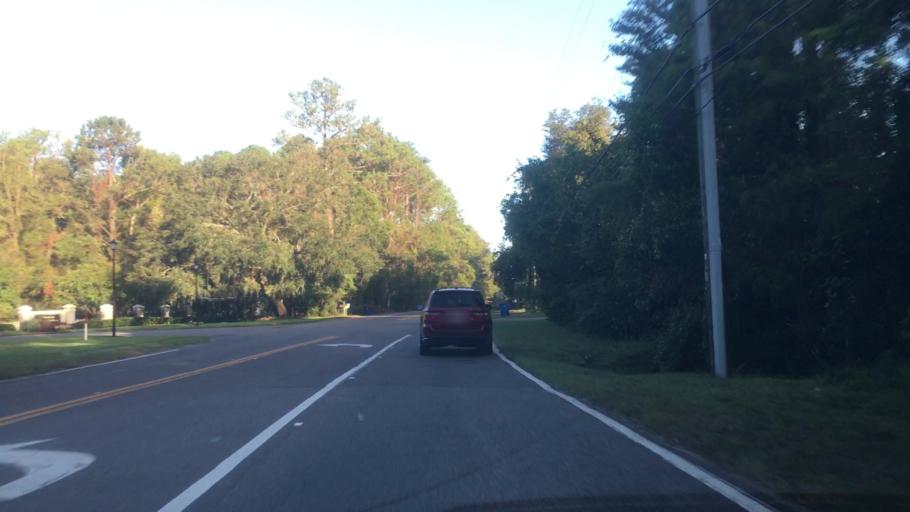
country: US
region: Florida
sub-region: Duval County
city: Jacksonville
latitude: 30.4668
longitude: -81.5979
